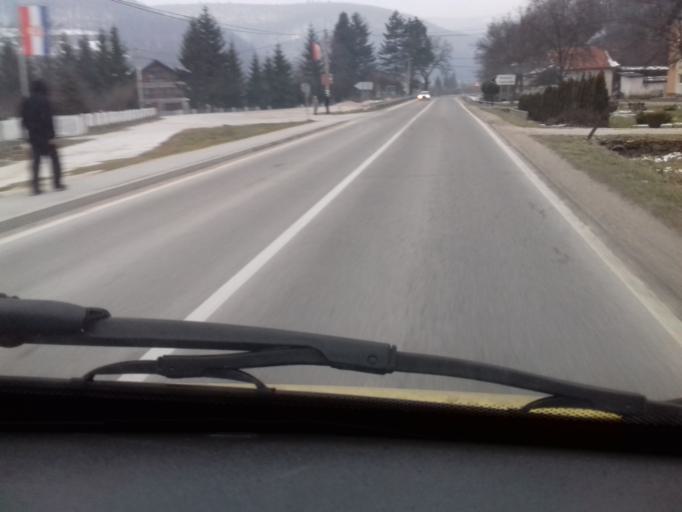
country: BA
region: Federation of Bosnia and Herzegovina
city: Novi Travnik
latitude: 44.1756
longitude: 17.6707
